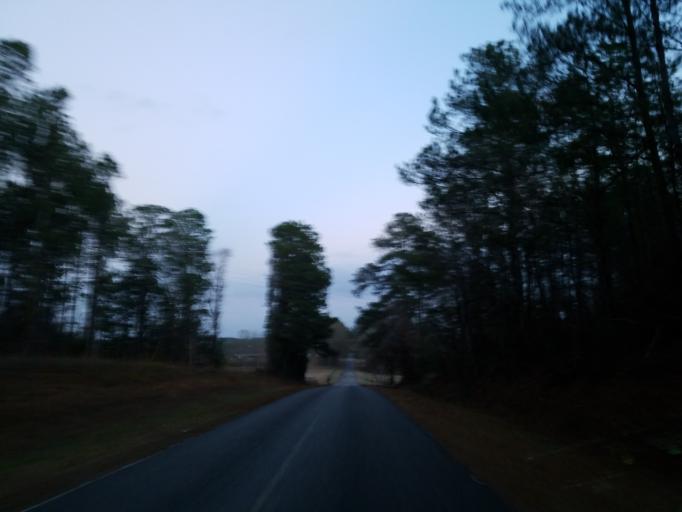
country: US
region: Alabama
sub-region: Sumter County
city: York
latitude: 32.4064
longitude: -88.4522
